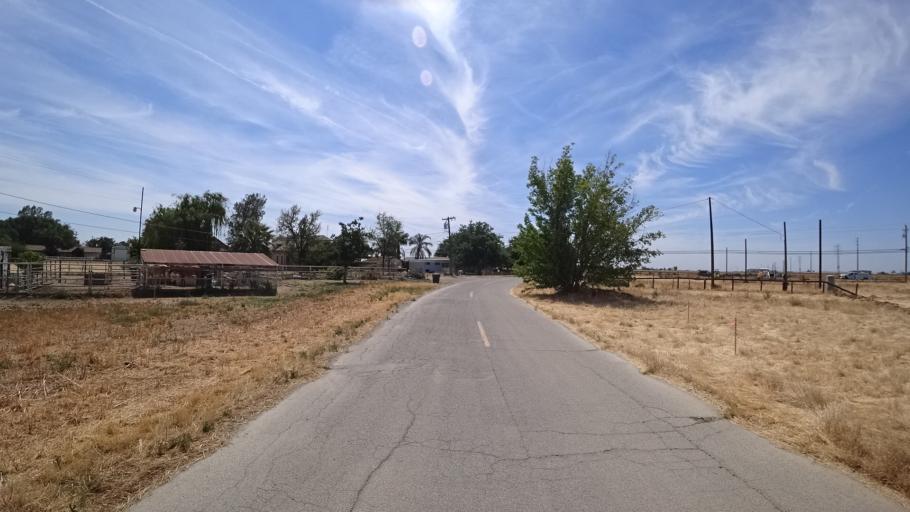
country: US
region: California
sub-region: Kings County
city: Home Garden
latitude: 36.3290
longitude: -119.5911
